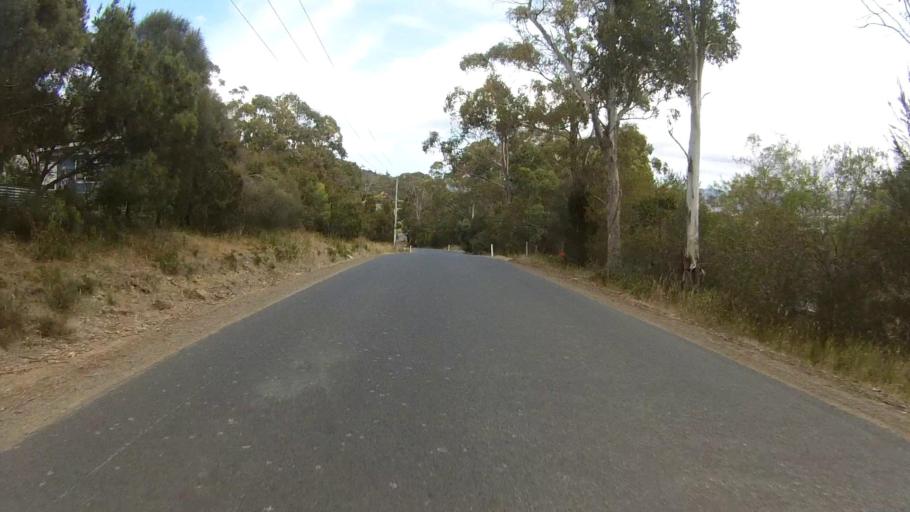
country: AU
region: Tasmania
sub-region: Kingborough
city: Blackmans Bay
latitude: -43.0290
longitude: 147.3121
